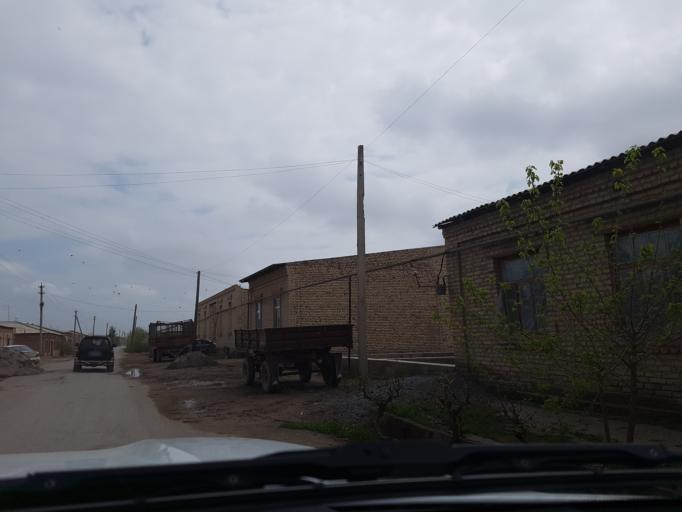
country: TM
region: Lebap
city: Turkmenabat
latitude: 38.9721
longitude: 63.6886
